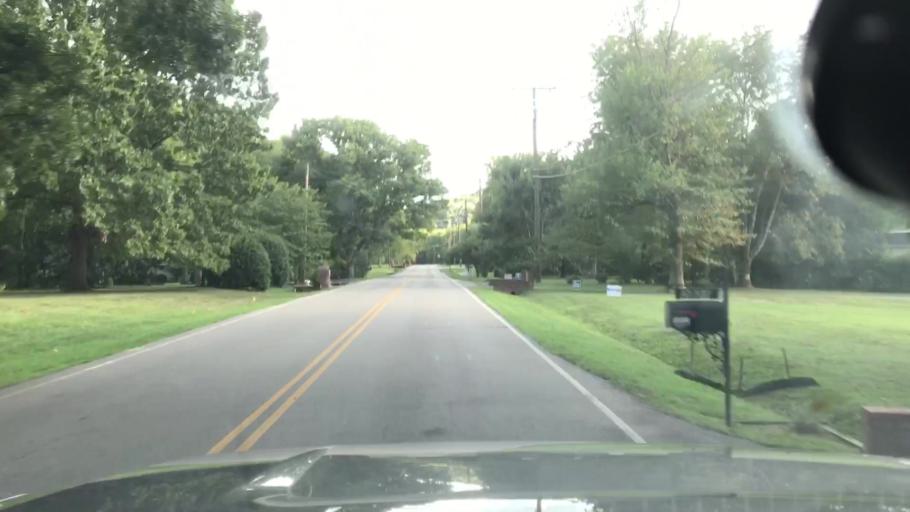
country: US
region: Tennessee
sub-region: Davidson County
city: Forest Hills
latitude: 36.0619
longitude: -86.8461
